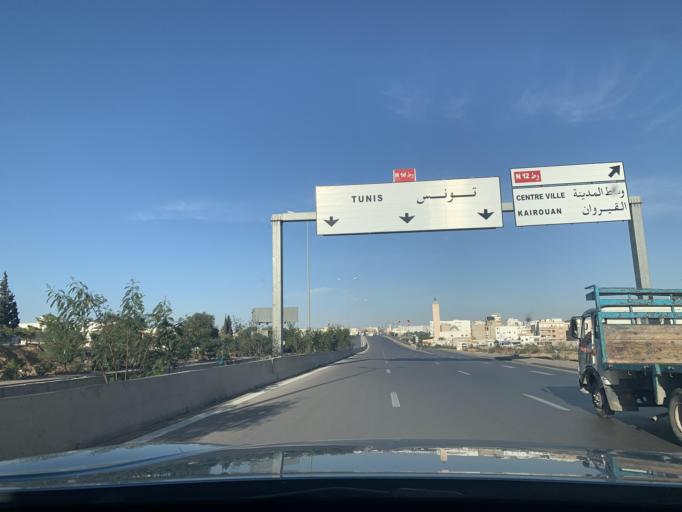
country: DZ
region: Souk Ahras
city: Souk Ahras
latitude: 36.3653
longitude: 8.0035
